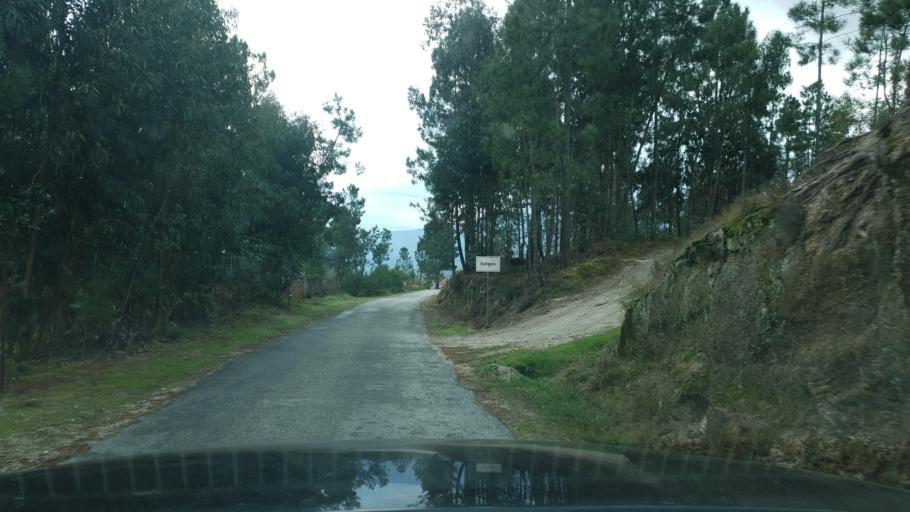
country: PT
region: Viseu
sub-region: Castro Daire
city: Castro Daire
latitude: 40.8805
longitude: -8.0096
